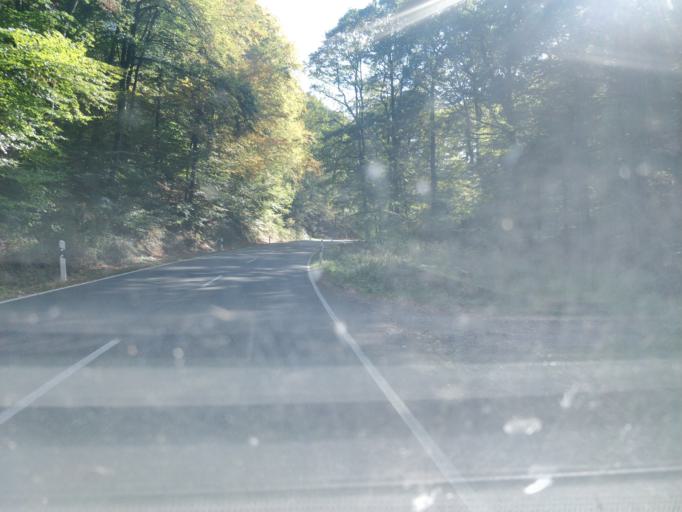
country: DE
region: North Rhine-Westphalia
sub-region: Regierungsbezirk Koln
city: Bad Munstereifel
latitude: 50.5557
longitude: 6.7990
